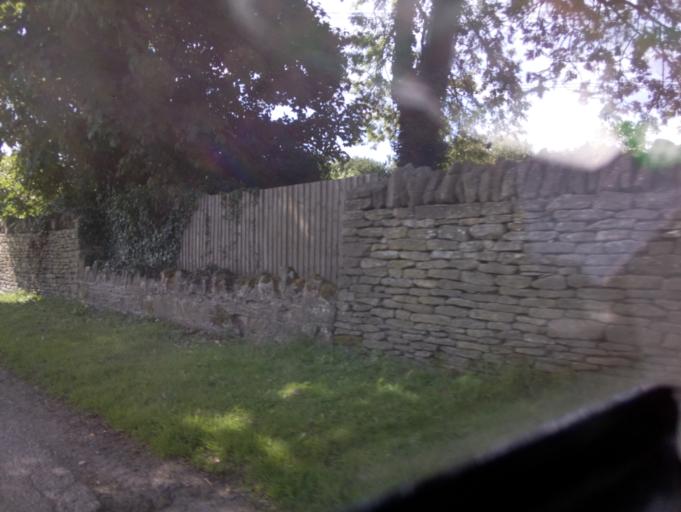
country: GB
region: England
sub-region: Wiltshire
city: Nettleton
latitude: 51.5087
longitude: -2.2626
